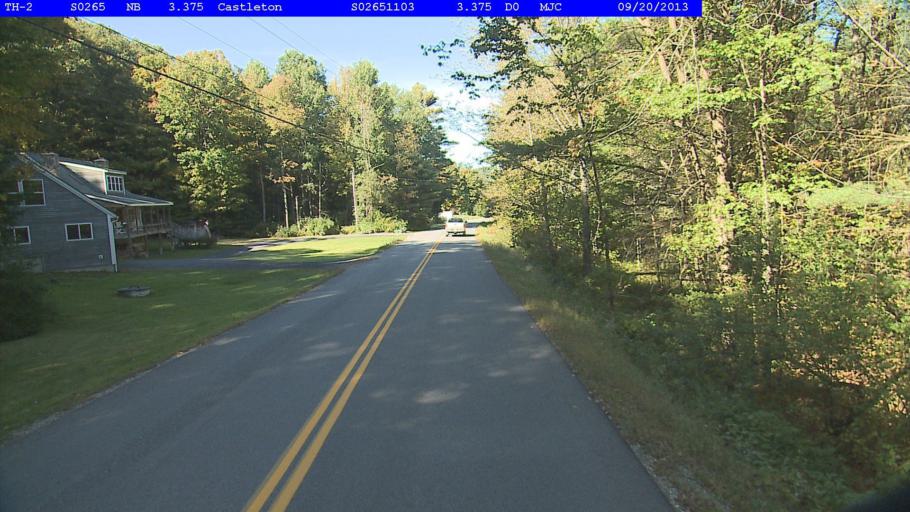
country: US
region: Vermont
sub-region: Rutland County
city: Fair Haven
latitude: 43.6491
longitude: -73.2318
